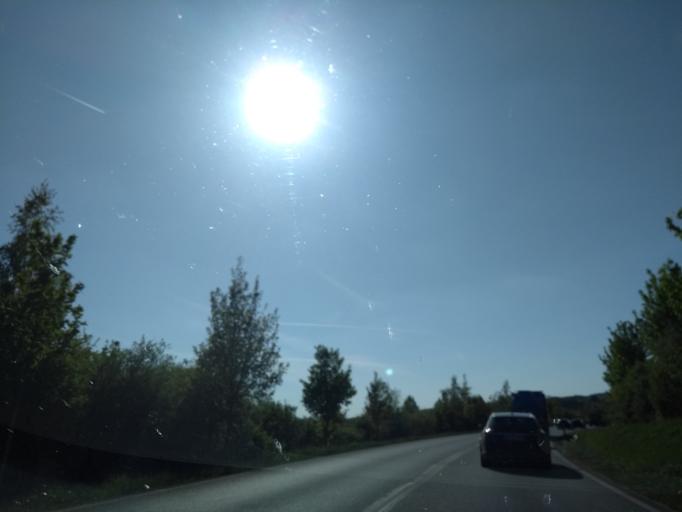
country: DE
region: Hesse
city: Frankenberg
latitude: 51.0417
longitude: 8.7560
